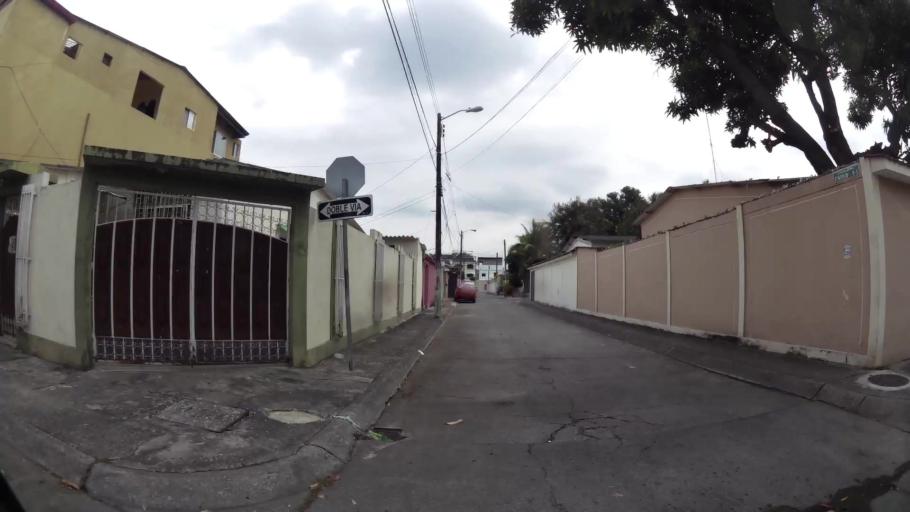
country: EC
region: Guayas
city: Eloy Alfaro
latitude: -2.1185
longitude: -79.8967
